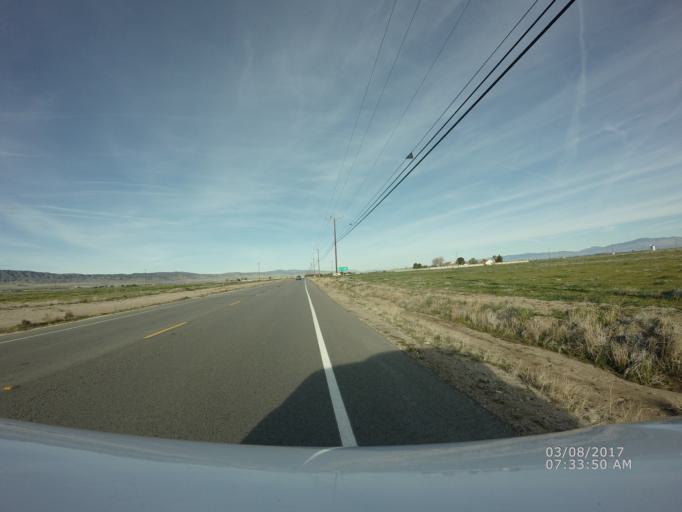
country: US
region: California
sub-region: Los Angeles County
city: Quartz Hill
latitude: 34.7040
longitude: -118.2698
